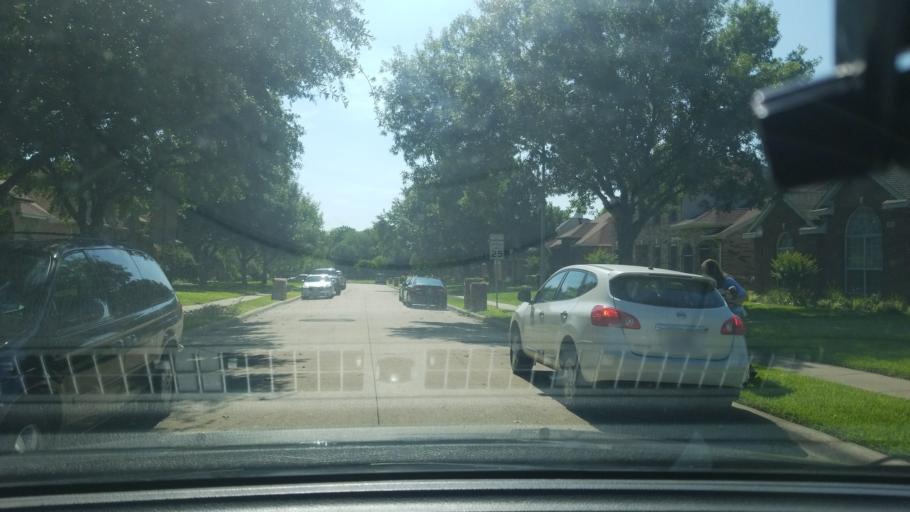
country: US
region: Texas
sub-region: Dallas County
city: Mesquite
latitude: 32.7749
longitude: -96.5821
